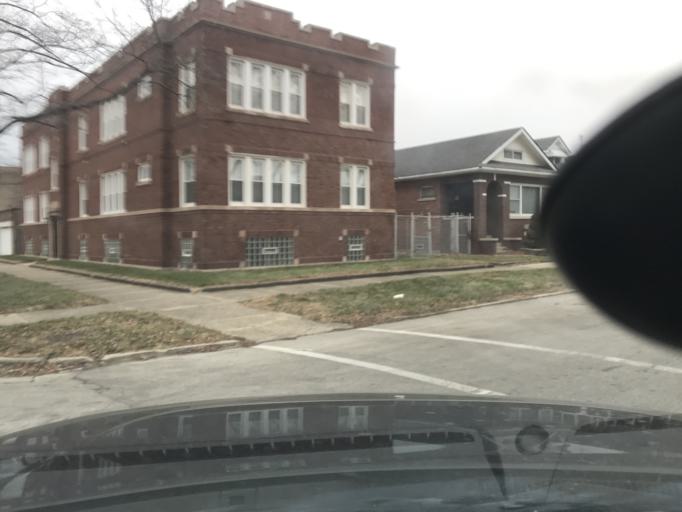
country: US
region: Indiana
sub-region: Lake County
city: Whiting
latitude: 41.7427
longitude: -87.5697
